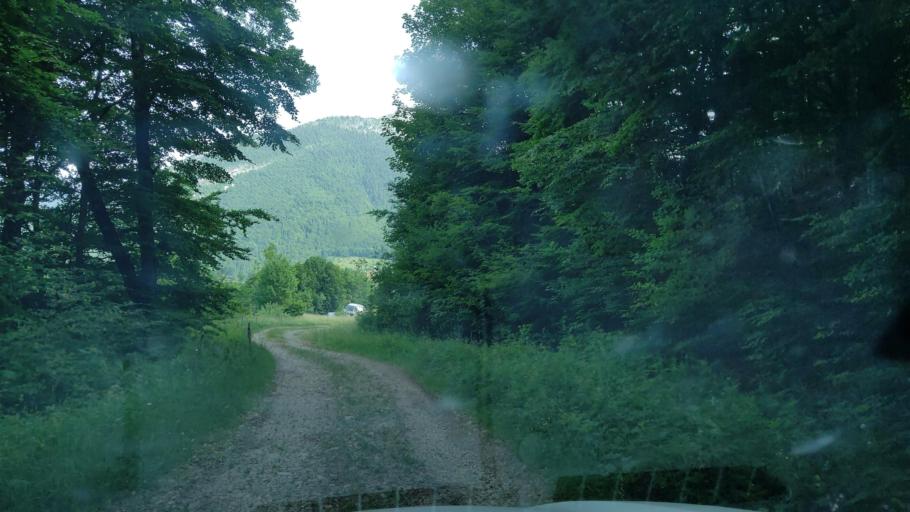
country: FR
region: Rhone-Alpes
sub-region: Departement de la Savoie
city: Cruet
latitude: 45.5989
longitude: 6.1075
